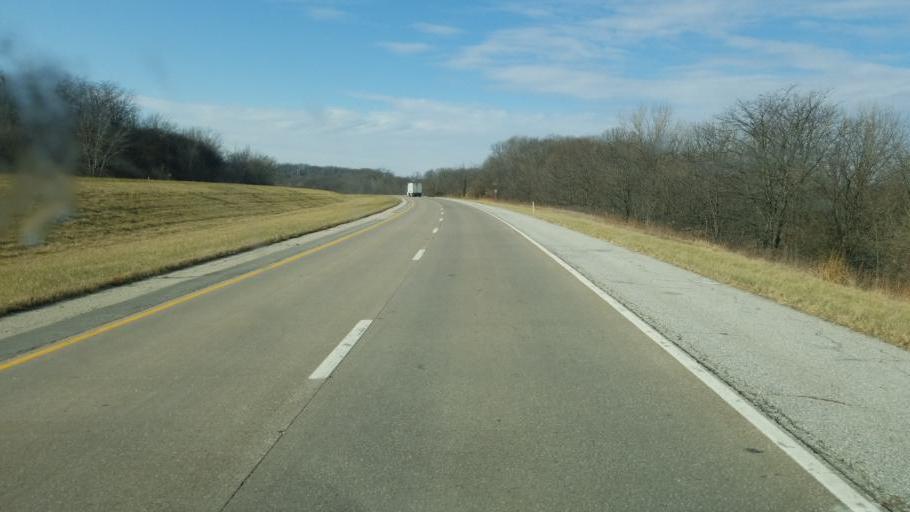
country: US
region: Illinois
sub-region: Warren County
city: Monmouth
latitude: 40.9242
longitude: -90.5558
